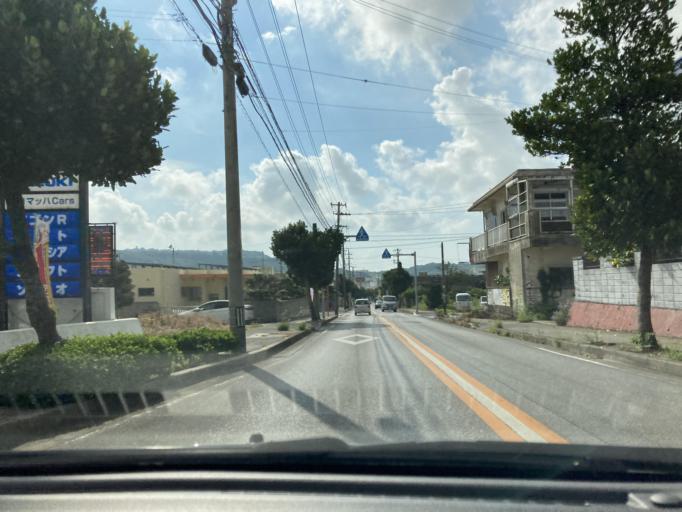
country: JP
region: Okinawa
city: Tomigusuku
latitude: 26.1593
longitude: 127.7464
